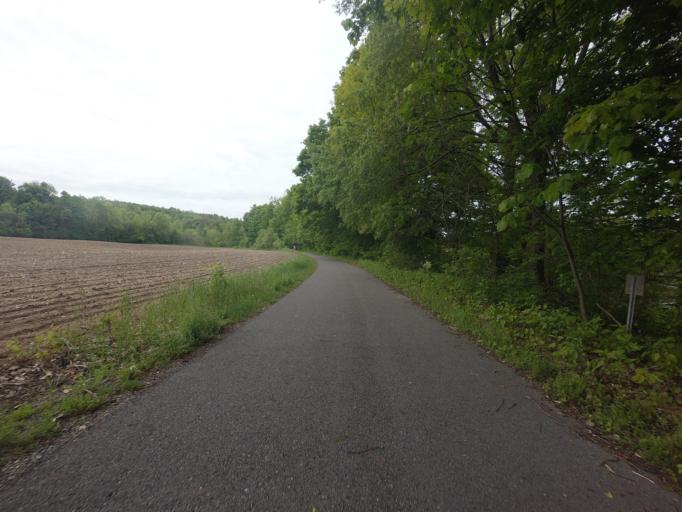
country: US
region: New York
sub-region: Jefferson County
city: Black River
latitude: 43.9956
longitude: -75.8215
